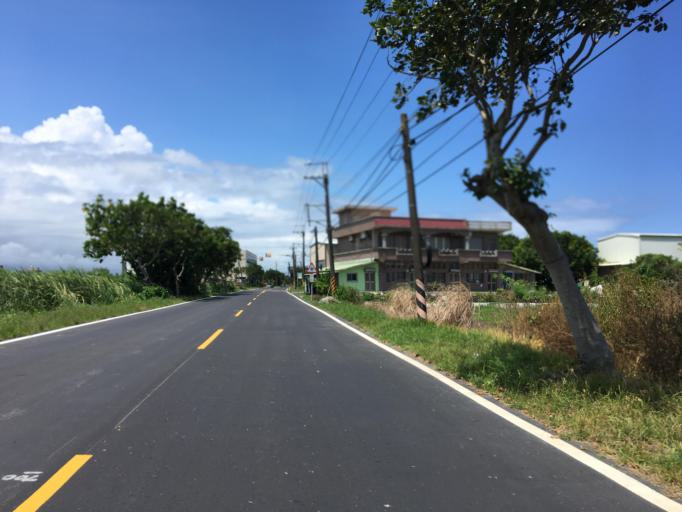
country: TW
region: Taiwan
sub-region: Yilan
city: Yilan
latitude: 24.6862
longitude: 121.8088
